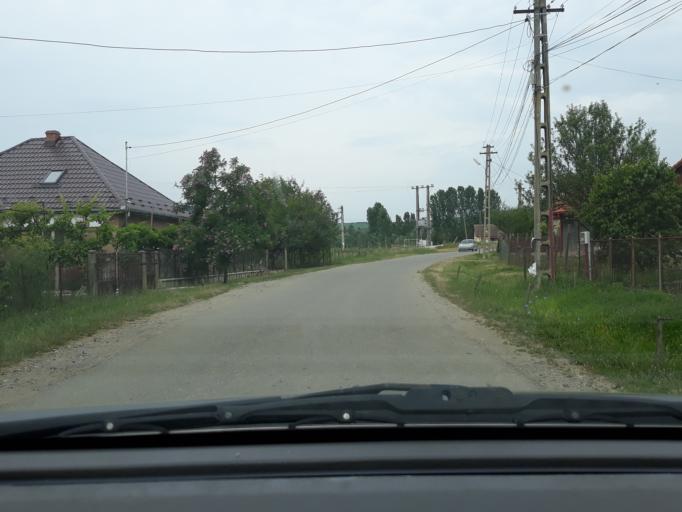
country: RO
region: Salaj
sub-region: Comuna Dobrin
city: Dobrin
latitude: 47.2886
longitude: 23.0968
